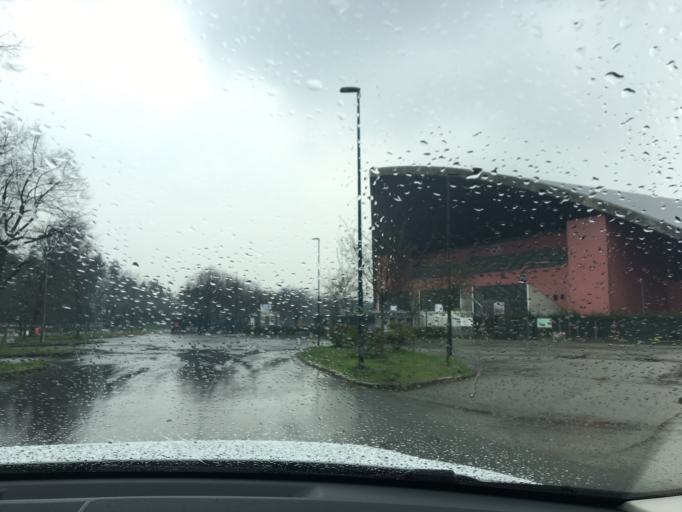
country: IT
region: Piedmont
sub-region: Provincia di Torino
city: Moncalieri
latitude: 45.0249
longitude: 7.6695
